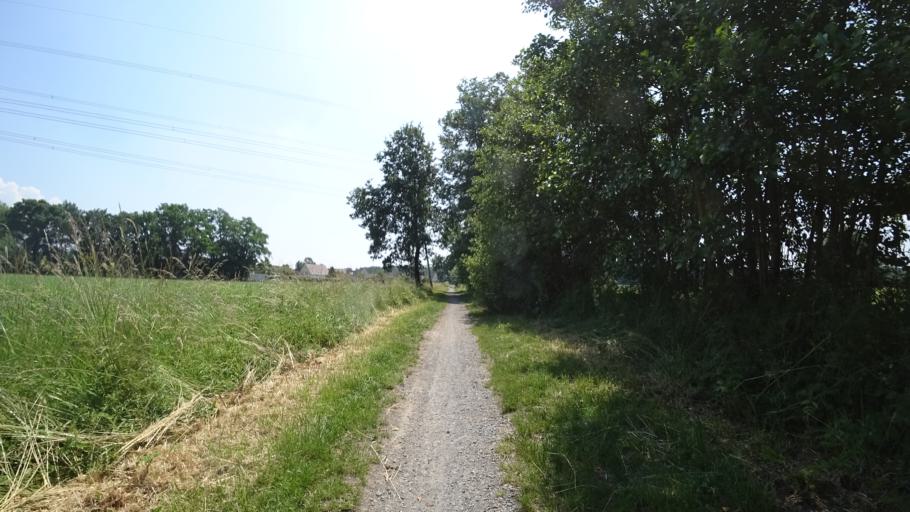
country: DE
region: North Rhine-Westphalia
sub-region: Regierungsbezirk Detmold
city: Guetersloh
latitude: 51.9318
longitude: 8.3741
